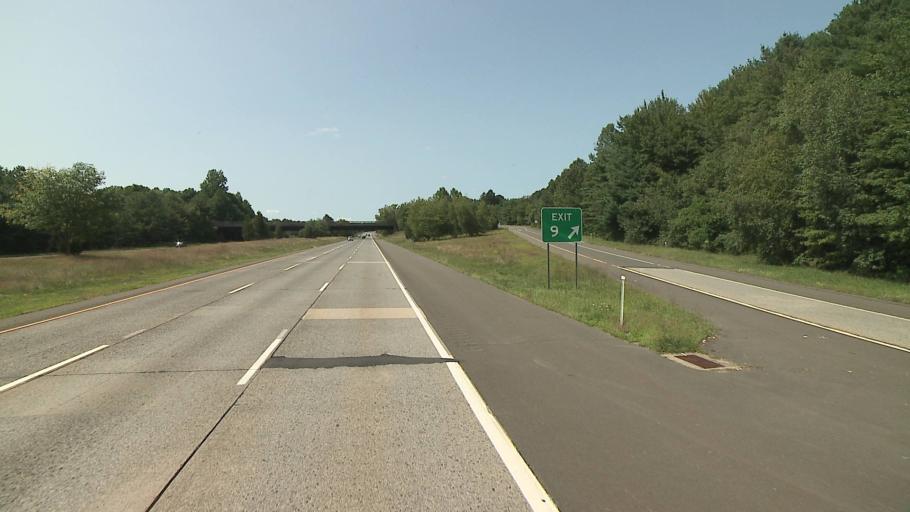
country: US
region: Connecticut
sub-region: Fairfield County
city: Trumbull
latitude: 41.2513
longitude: -73.1951
